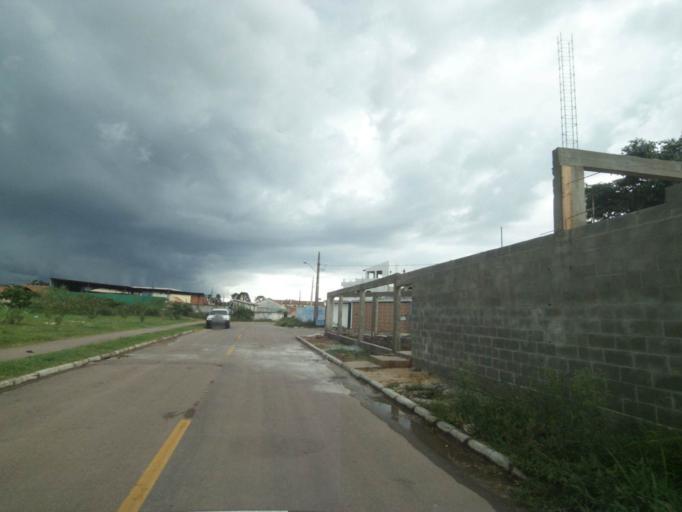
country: BR
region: Parana
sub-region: Pinhais
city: Pinhais
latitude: -25.4713
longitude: -49.1876
